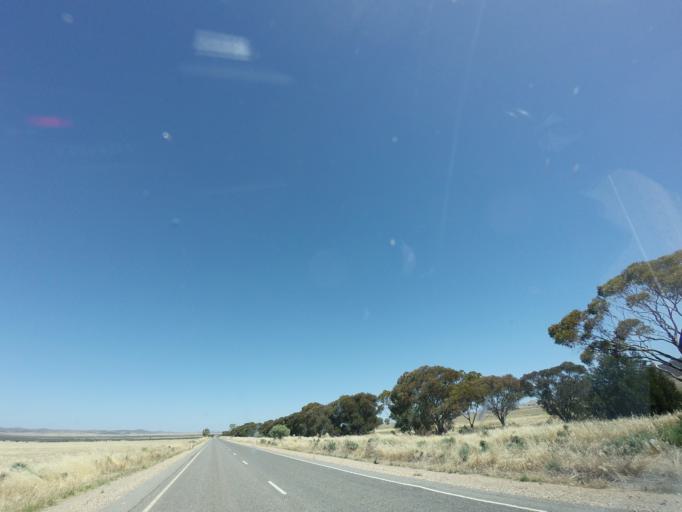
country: AU
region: South Australia
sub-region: Peterborough
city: Peterborough
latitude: -32.7552
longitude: 138.6454
